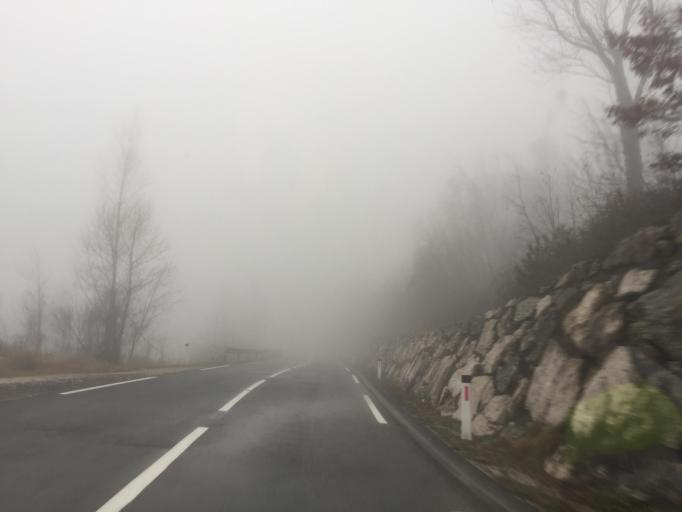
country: SI
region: Ajdovscina
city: Lokavec
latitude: 45.9351
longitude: 13.8774
